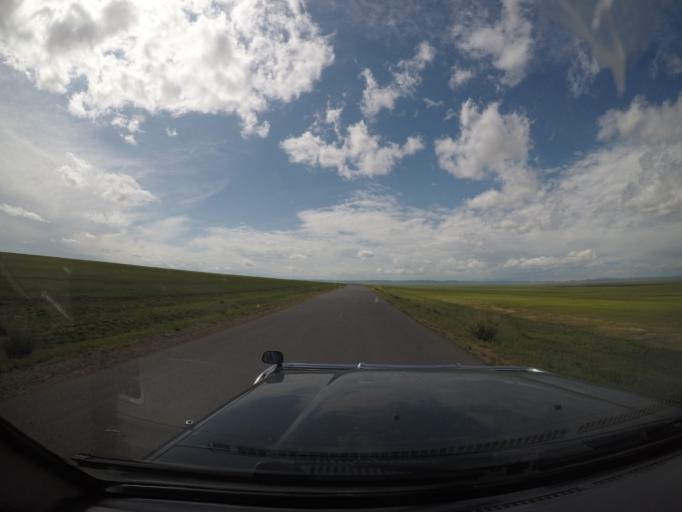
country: MN
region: Hentiy
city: Moron
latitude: 47.4224
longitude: 110.1497
